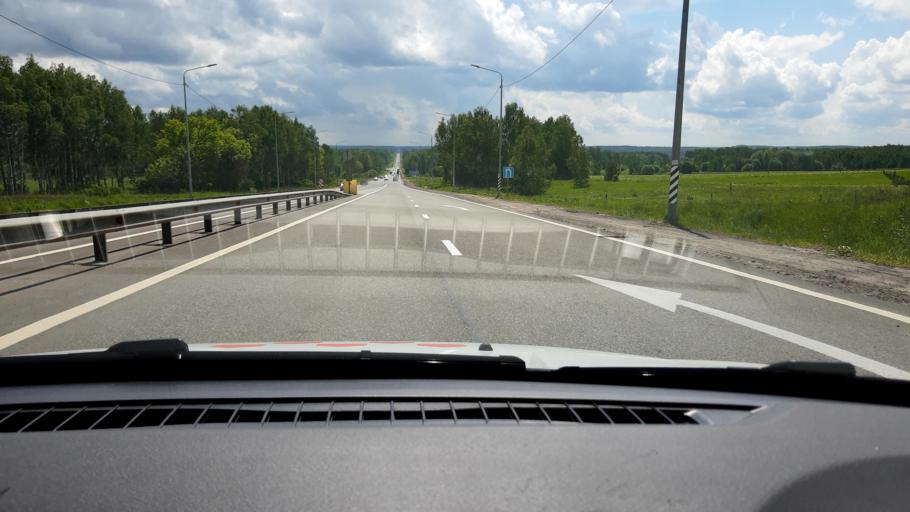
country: RU
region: Nizjnij Novgorod
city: Dal'neye Konstantinovo
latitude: 55.9916
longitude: 43.9689
